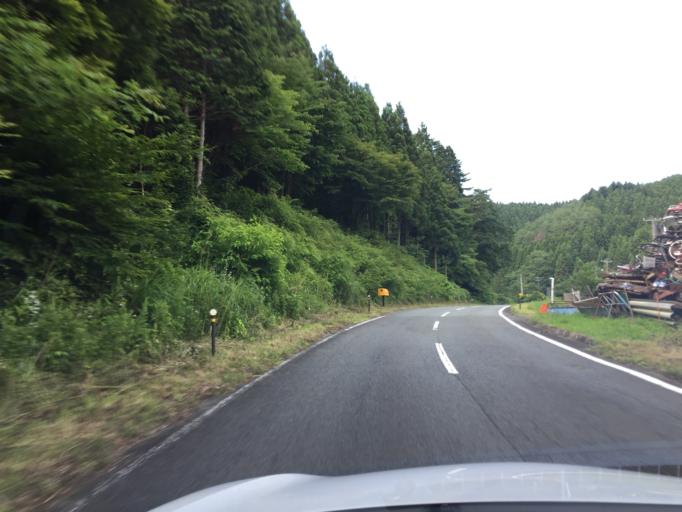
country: JP
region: Fukushima
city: Ishikawa
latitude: 37.1288
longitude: 140.6416
